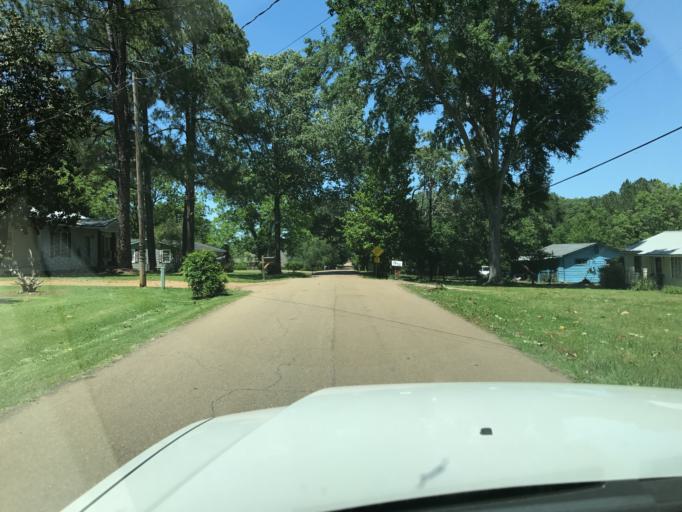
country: US
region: Mississippi
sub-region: Madison County
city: Ridgeland
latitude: 32.4314
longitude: -90.1335
